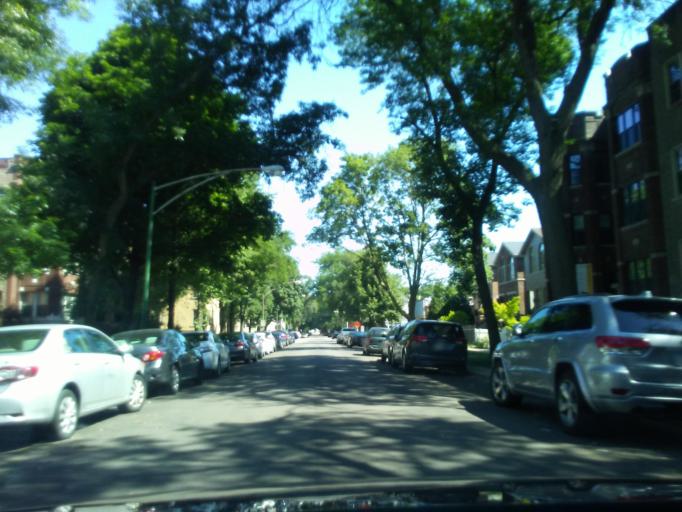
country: US
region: Illinois
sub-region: Cook County
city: Lincolnwood
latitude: 41.9750
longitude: -87.6778
